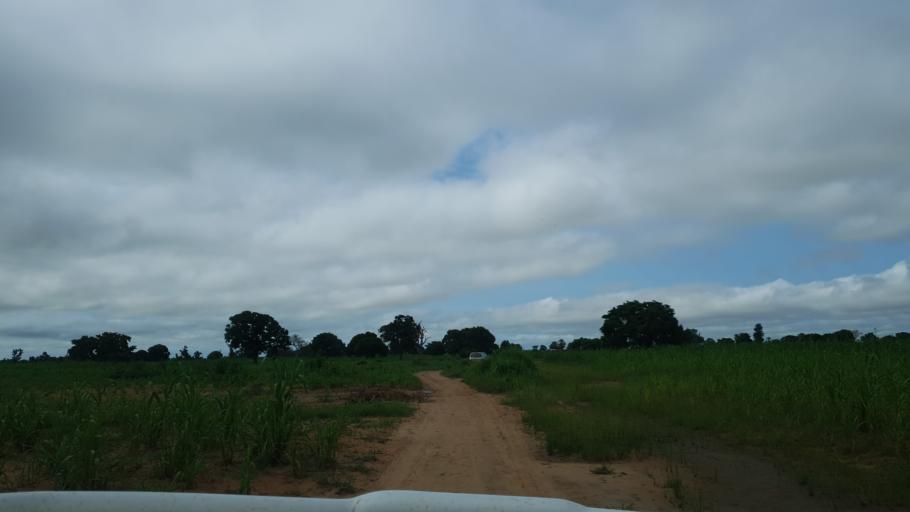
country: ML
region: Segou
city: Baroueli
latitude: 13.4934
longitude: -6.8964
